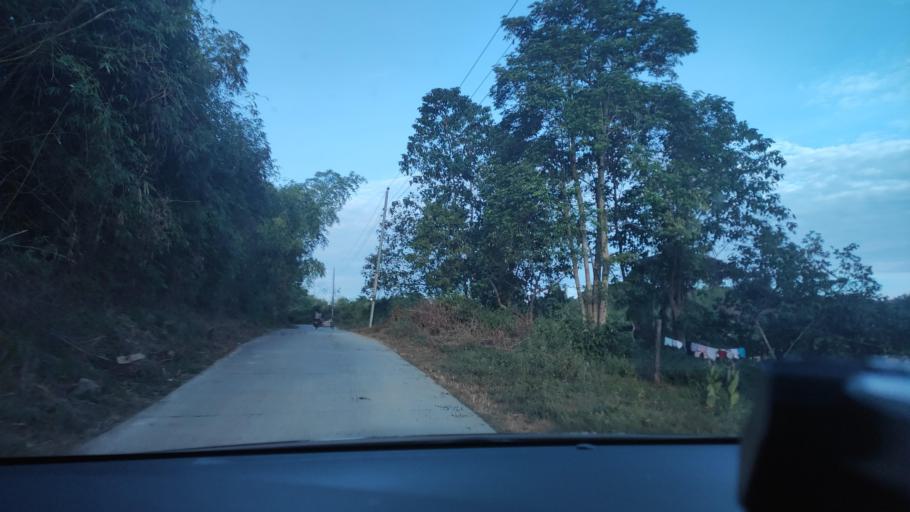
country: PH
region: Ilocos
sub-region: Province of Pangasinan
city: Balingasay
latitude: 16.3062
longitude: 119.8591
